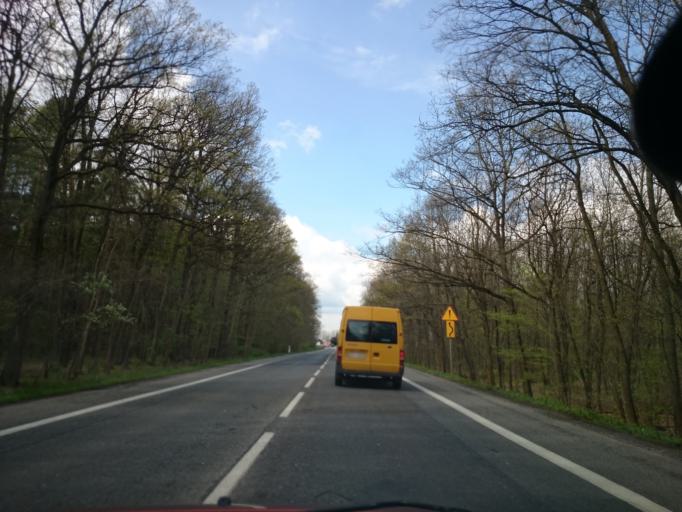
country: PL
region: Opole Voivodeship
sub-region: Powiat opolski
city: Tarnow Opolski
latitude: 50.5976
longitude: 18.0889
